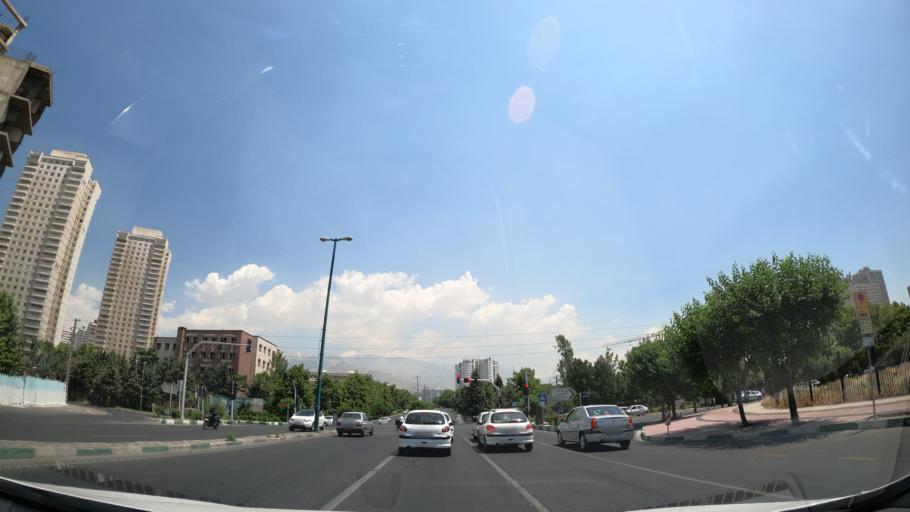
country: IR
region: Tehran
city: Tajrish
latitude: 35.7614
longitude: 51.3756
